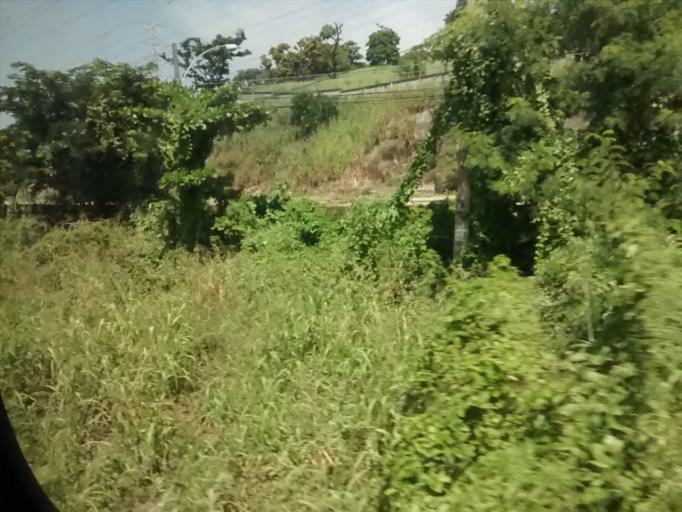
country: BR
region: Rio de Janeiro
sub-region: Rio De Janeiro
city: Rio de Janeiro
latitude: -22.8732
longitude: -43.2538
